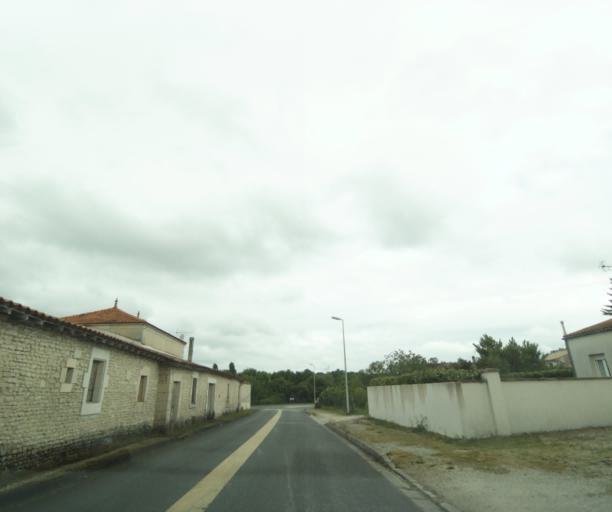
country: FR
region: Poitou-Charentes
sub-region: Departement de la Charente-Maritime
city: Cherac
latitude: 45.6873
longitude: -0.4987
